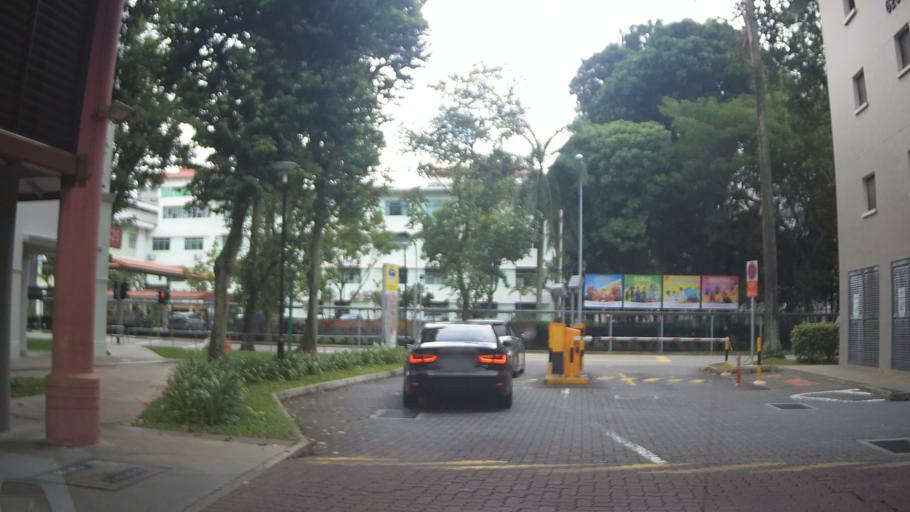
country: MY
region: Johor
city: Johor Bahru
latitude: 1.3985
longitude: 103.7465
